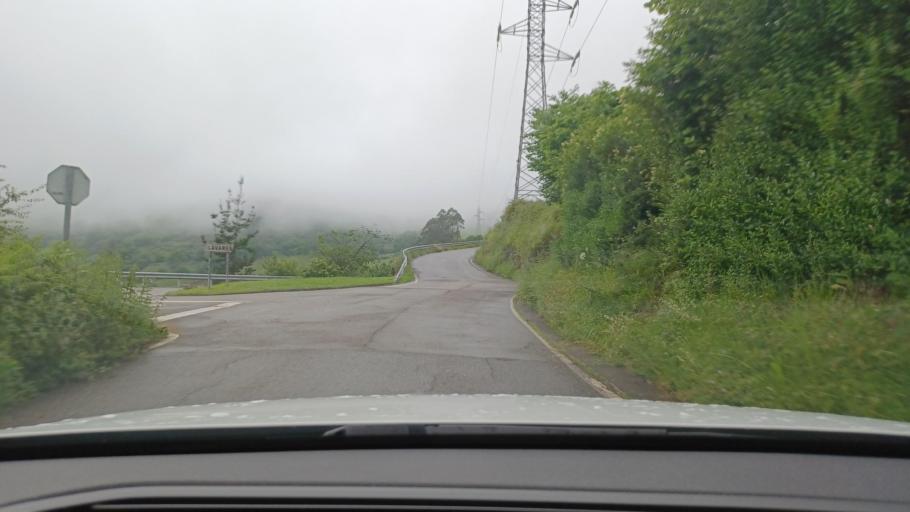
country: ES
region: Asturias
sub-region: Province of Asturias
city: Castandiello
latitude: 43.2955
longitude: -5.9575
